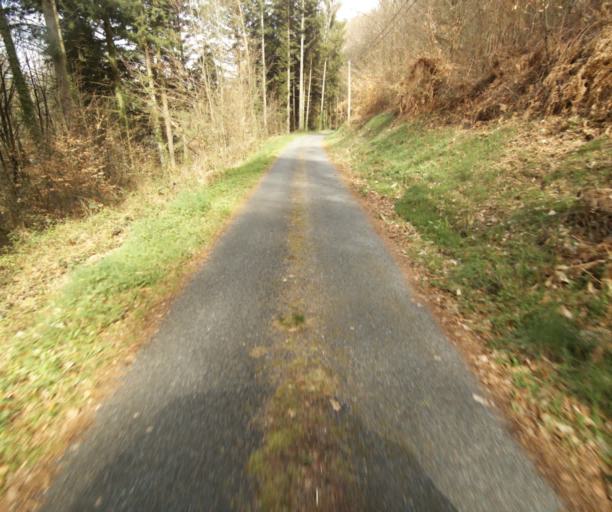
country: FR
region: Limousin
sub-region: Departement de la Correze
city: Correze
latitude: 45.3556
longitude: 1.8797
